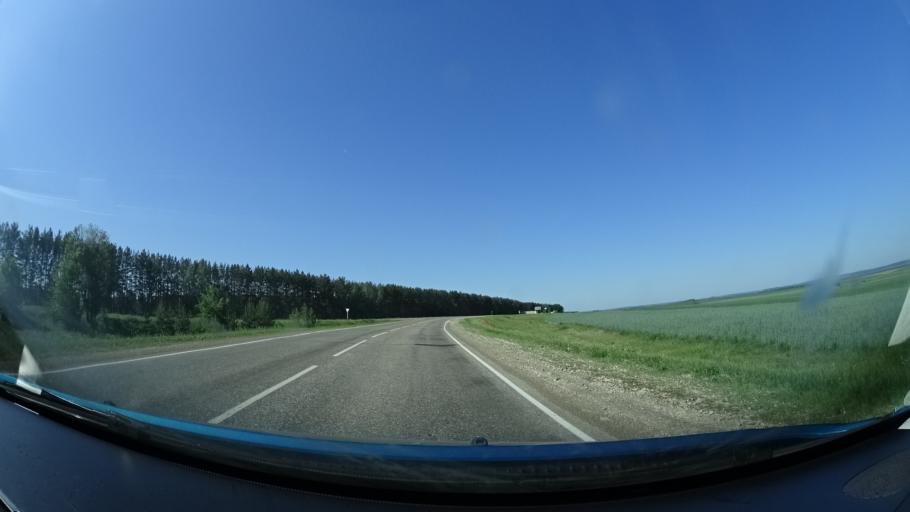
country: RU
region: Bashkortostan
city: Starobaltachevo
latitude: 55.9342
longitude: 55.8260
